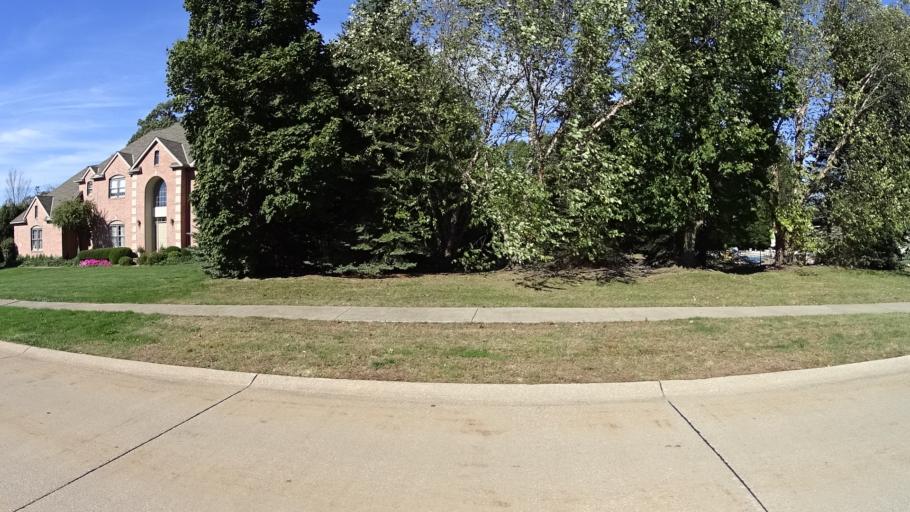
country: US
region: Ohio
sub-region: Lorain County
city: Amherst
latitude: 41.3890
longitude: -82.2364
